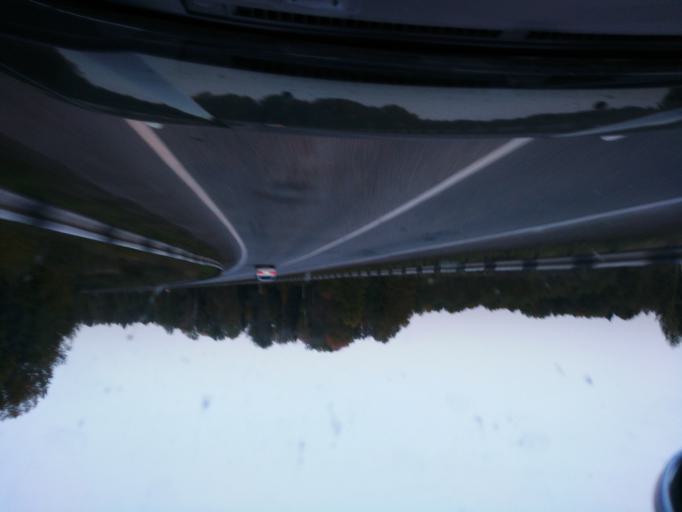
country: RU
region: Perm
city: Verkhnechusovskiye Gorodki
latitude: 58.2932
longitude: 56.8921
